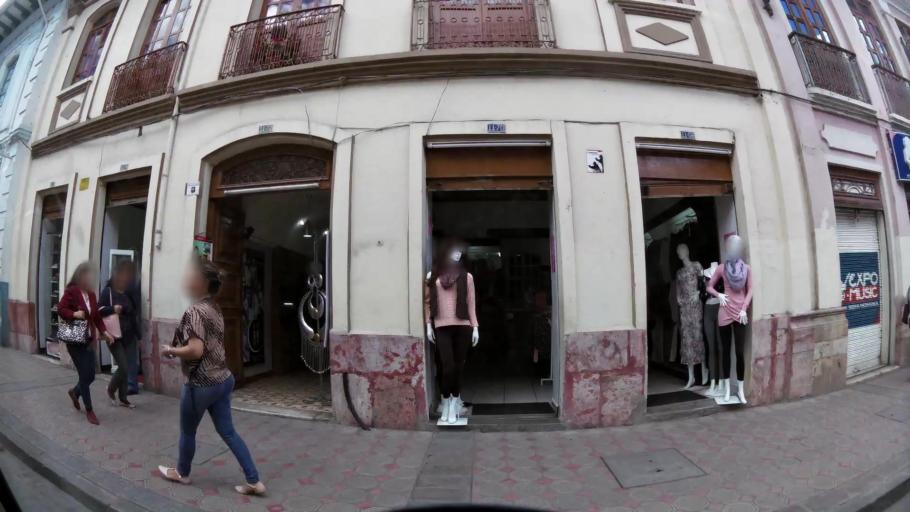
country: EC
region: Azuay
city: Cuenca
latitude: -2.8944
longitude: -79.0034
